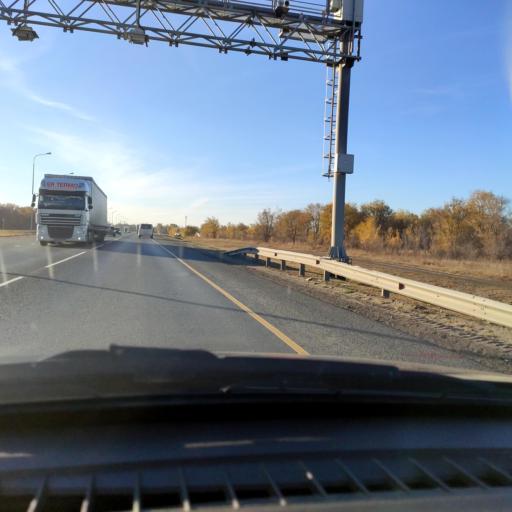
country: RU
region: Samara
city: Varlamovo
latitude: 53.1912
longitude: 48.3489
